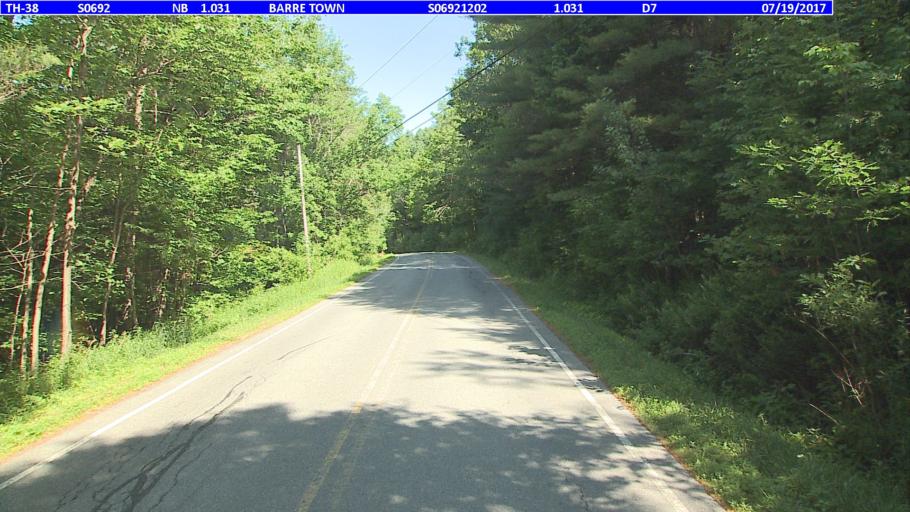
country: US
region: Vermont
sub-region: Washington County
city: South Barre
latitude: 44.1729
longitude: -72.4569
